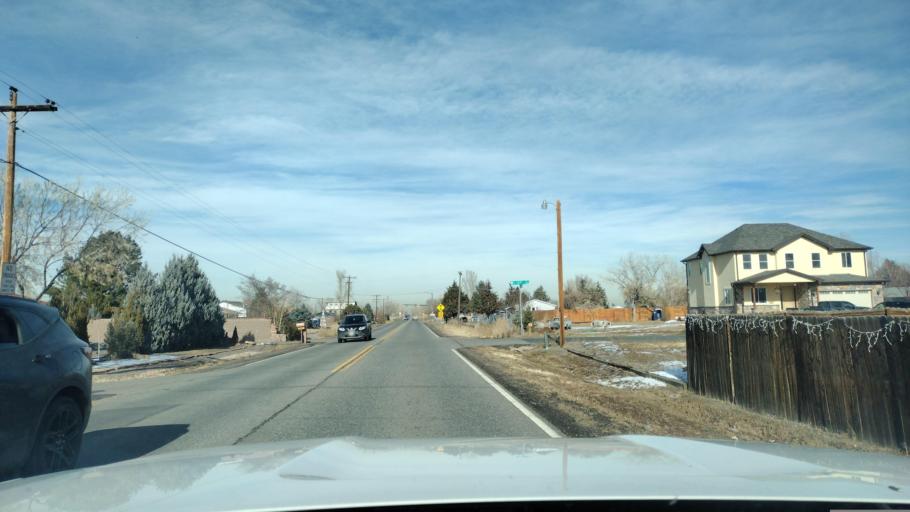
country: US
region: Colorado
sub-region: Adams County
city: Brighton
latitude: 39.9405
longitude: -104.8183
